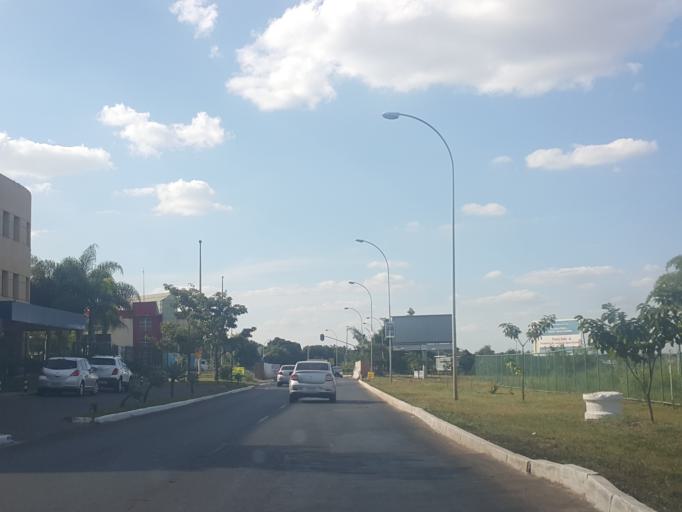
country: BR
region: Federal District
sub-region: Brasilia
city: Brasilia
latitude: -15.8375
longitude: -48.0083
